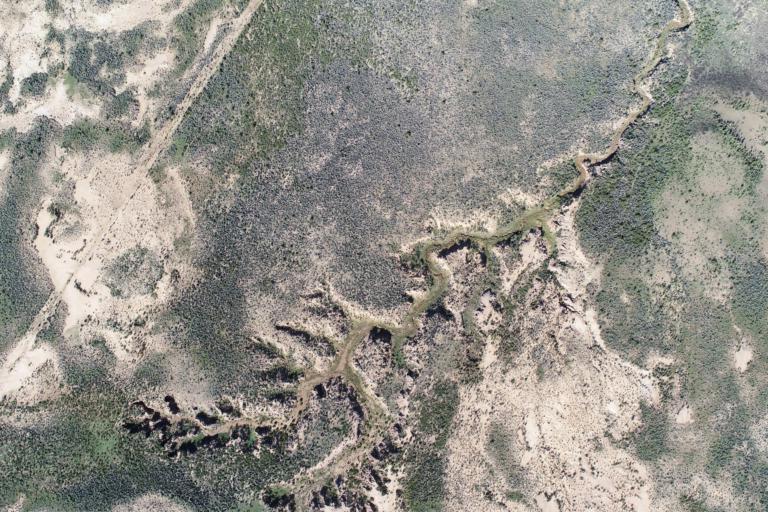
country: BO
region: La Paz
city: Curahuara de Carangas
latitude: -17.3020
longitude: -68.5133
